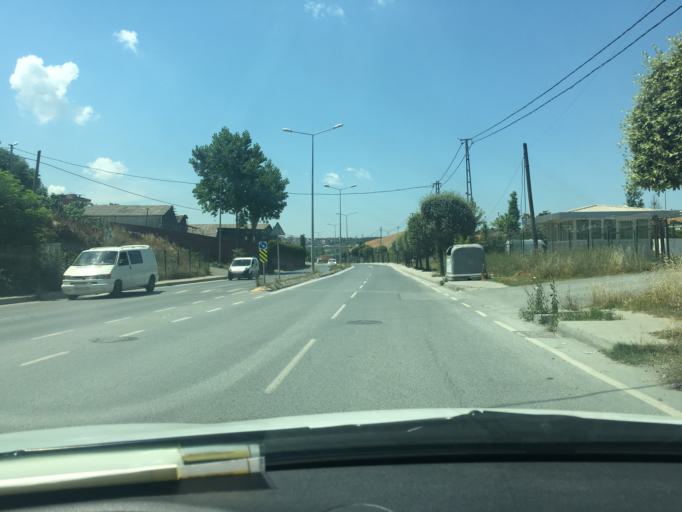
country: TR
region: Istanbul
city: Sisli
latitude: 41.0879
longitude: 28.9350
